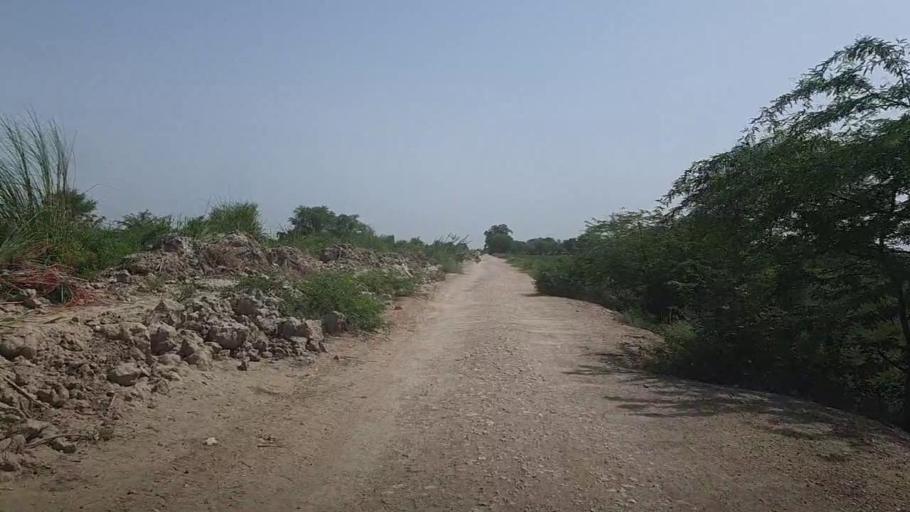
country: PK
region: Sindh
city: Pad Idan
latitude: 26.7901
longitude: 68.3272
